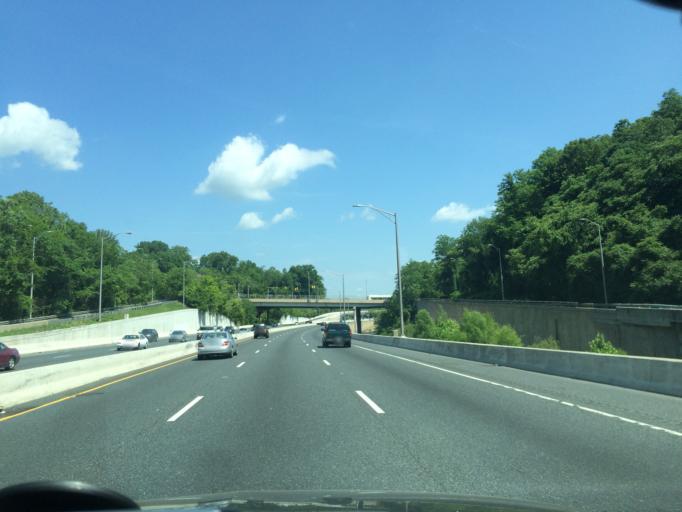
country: US
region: Maryland
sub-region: Baltimore County
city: Towson
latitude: 39.3580
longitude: -76.6500
